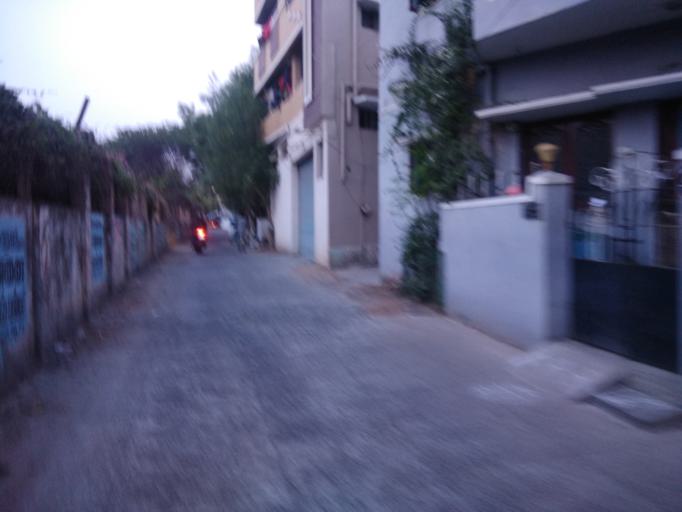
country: IN
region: Tamil Nadu
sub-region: Kancheepuram
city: Alandur
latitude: 13.0114
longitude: 80.2255
